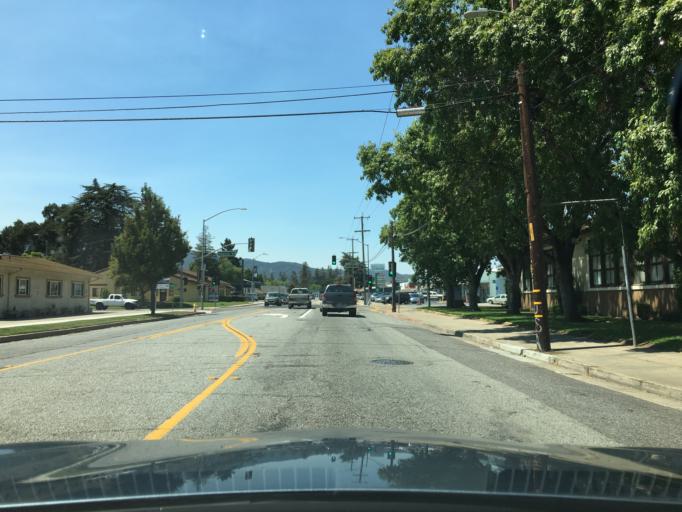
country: US
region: California
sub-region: Santa Clara County
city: Gilroy
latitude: 37.0142
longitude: -121.5738
